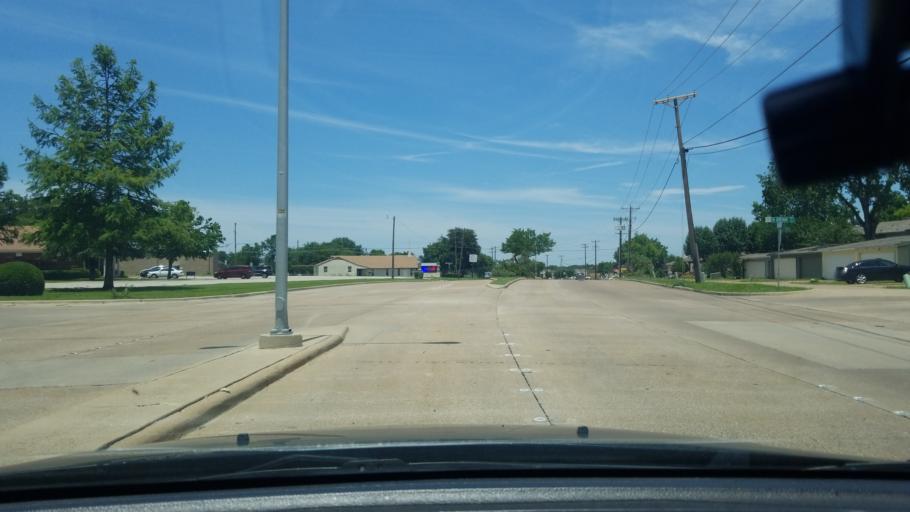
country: US
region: Texas
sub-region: Dallas County
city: Mesquite
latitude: 32.7794
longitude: -96.5969
